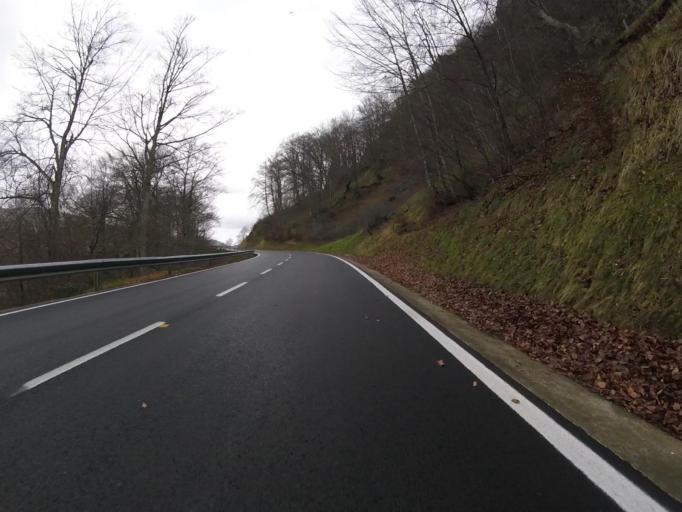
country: ES
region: Navarre
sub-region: Provincia de Navarra
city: Arbizu
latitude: 42.8631
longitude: -2.0145
